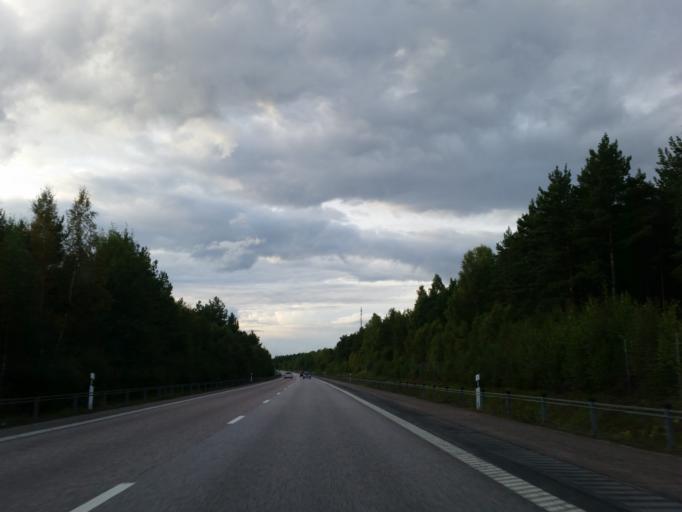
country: SE
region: Stockholm
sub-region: Sigtuna Kommun
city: Marsta
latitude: 59.6603
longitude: 17.8845
